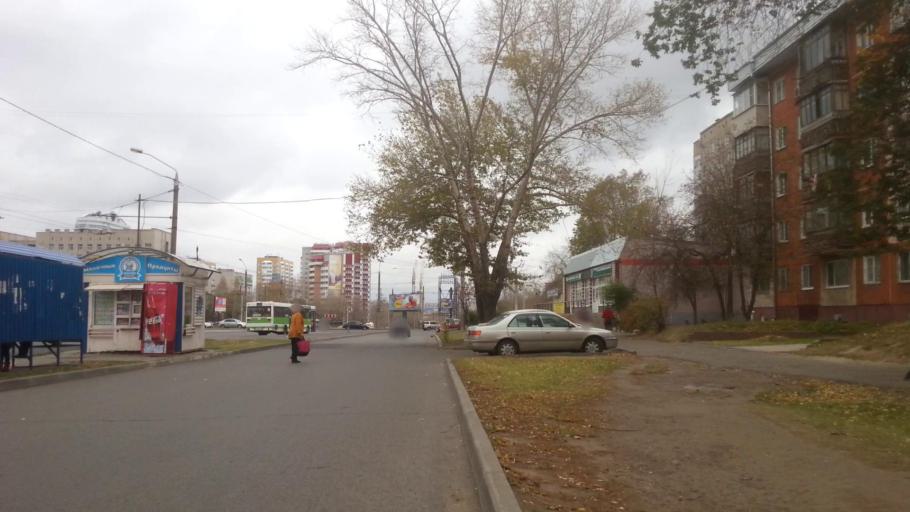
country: RU
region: Altai Krai
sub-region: Gorod Barnaulskiy
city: Barnaul
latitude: 53.3664
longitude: 83.7067
